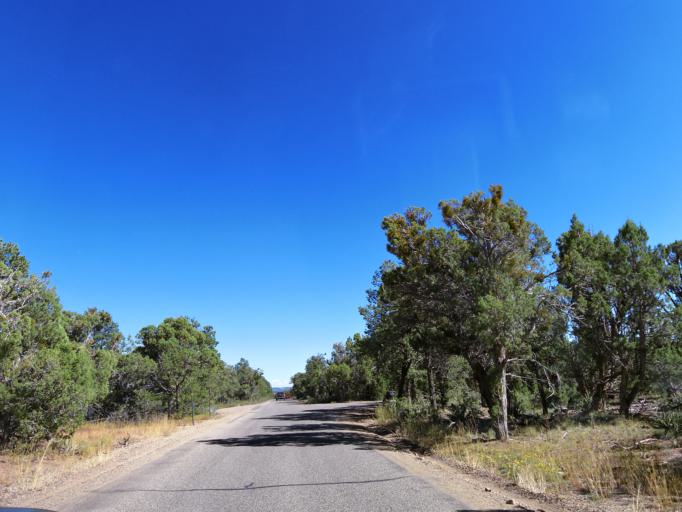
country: US
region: Colorado
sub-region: Montezuma County
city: Cortez
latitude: 37.1649
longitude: -108.4860
